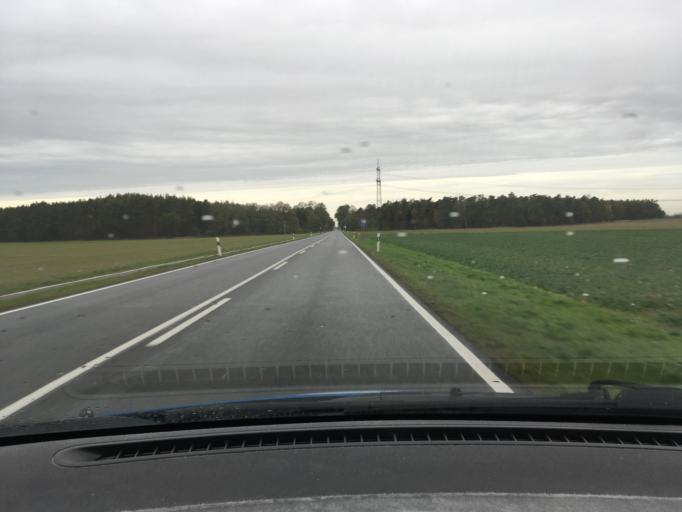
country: DE
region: Saxony-Anhalt
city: Zerbst
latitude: 51.9408
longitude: 12.1200
